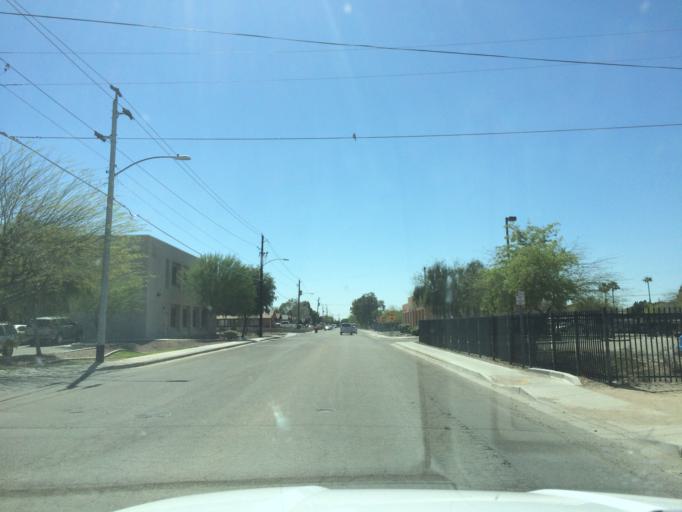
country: US
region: Arizona
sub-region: Yuma County
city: Yuma
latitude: 32.6960
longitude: -114.6225
